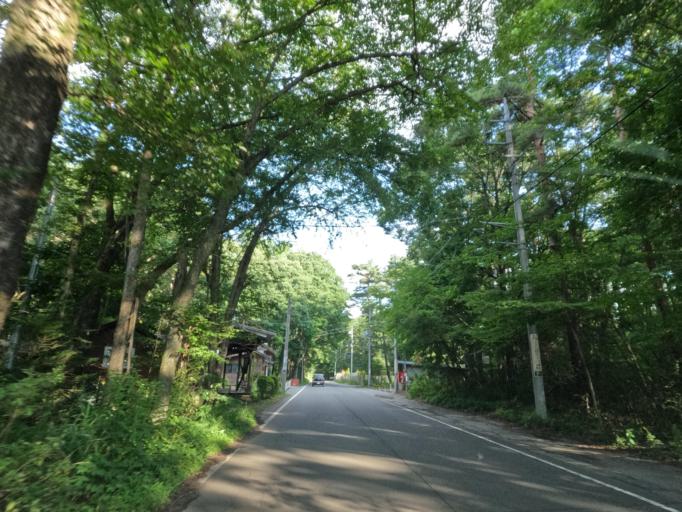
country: JP
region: Nagano
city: Komoro
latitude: 36.4684
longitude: 138.5670
